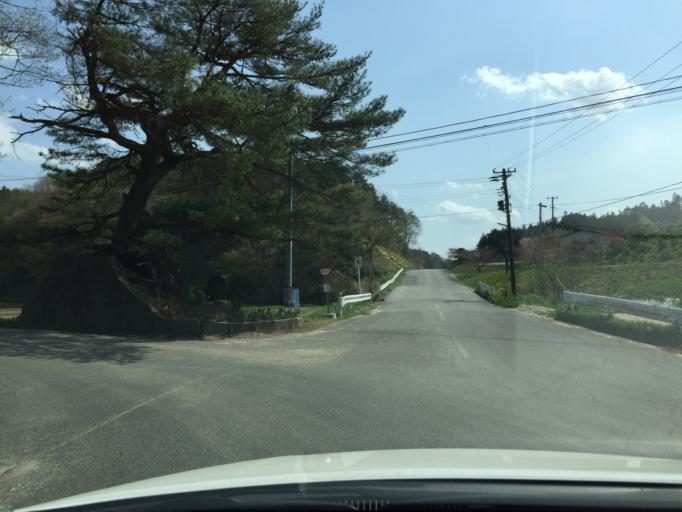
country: JP
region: Fukushima
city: Namie
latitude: 37.4001
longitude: 140.8019
